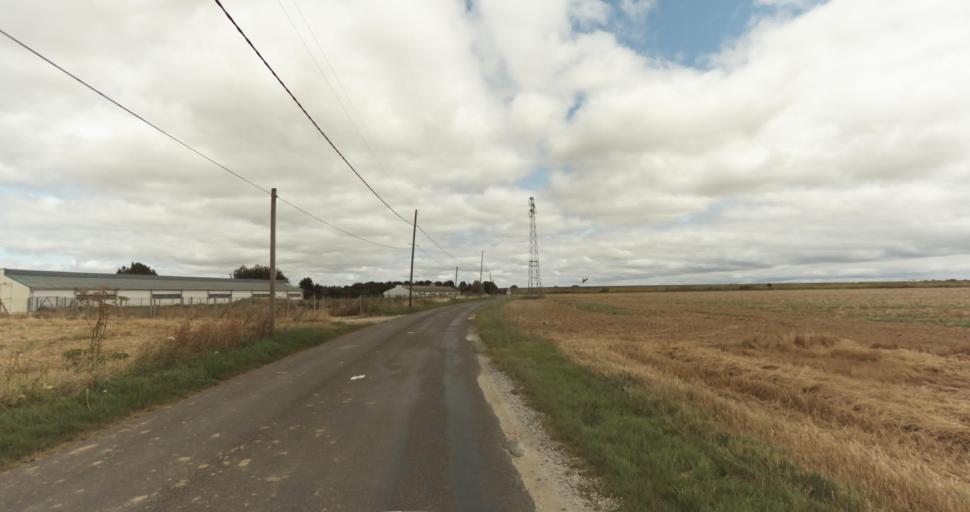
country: FR
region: Haute-Normandie
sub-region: Departement de l'Eure
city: Evreux
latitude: 48.9463
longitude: 1.2007
